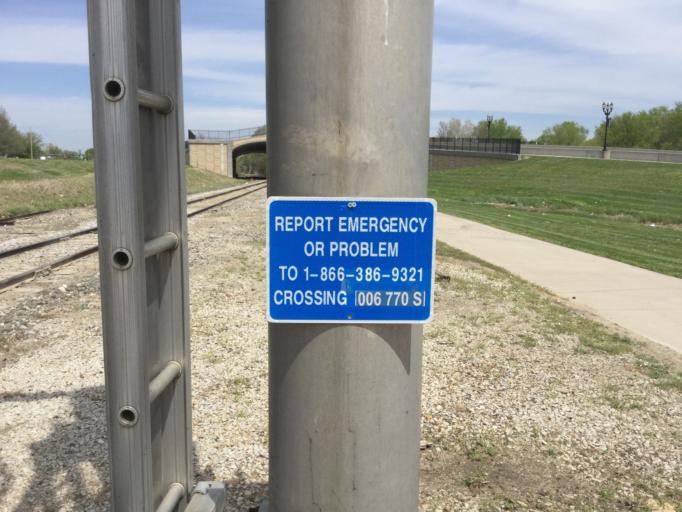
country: US
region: Kansas
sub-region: Neosho County
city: Chanute
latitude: 37.6846
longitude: -95.4525
